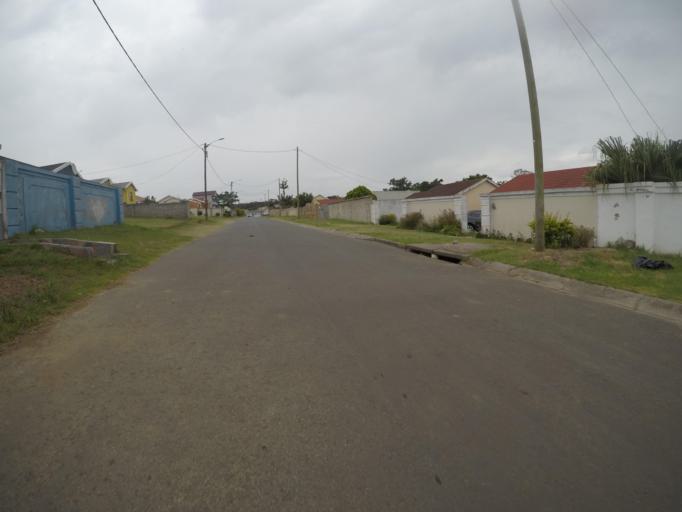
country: ZA
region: Eastern Cape
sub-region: Buffalo City Metropolitan Municipality
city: East London
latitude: -32.9942
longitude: 27.8468
